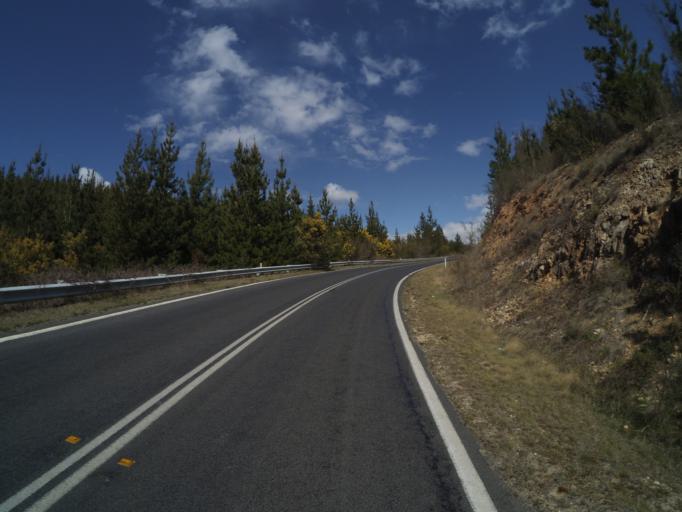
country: AU
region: Australian Capital Territory
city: Macquarie
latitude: -35.3699
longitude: 148.9620
